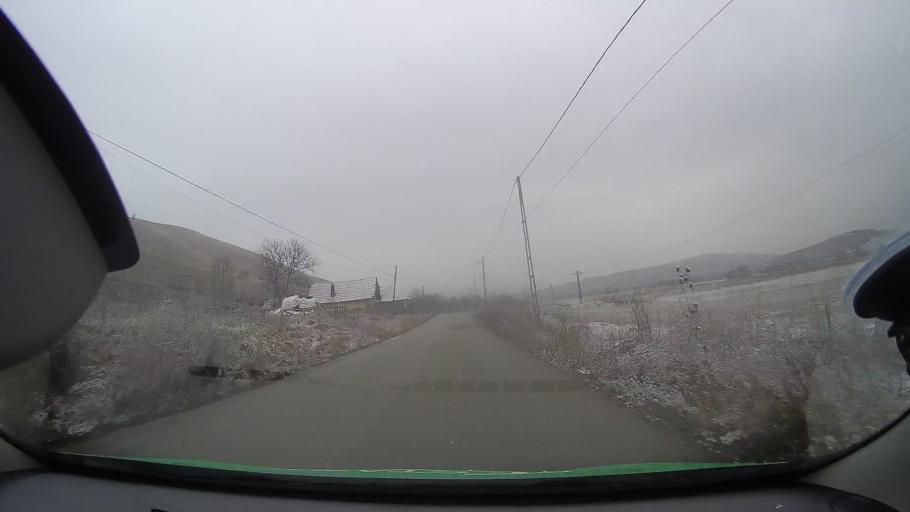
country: RO
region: Alba
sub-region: Comuna Noslac
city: Noslac
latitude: 46.3396
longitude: 23.9502
